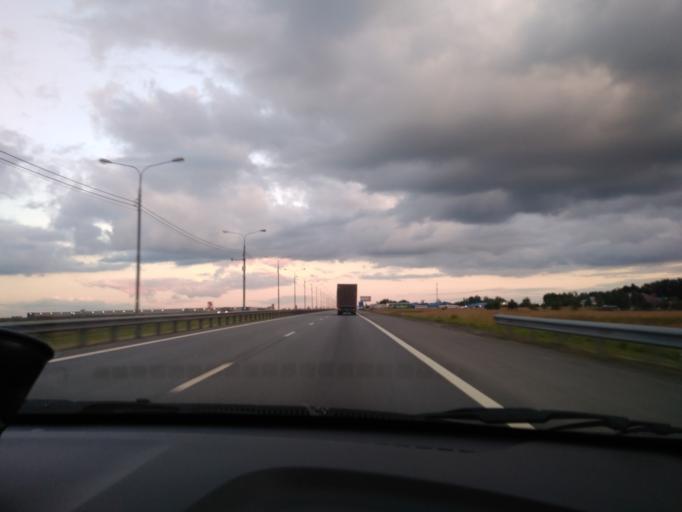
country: RU
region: Moskovskaya
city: Zhukovskiy
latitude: 55.4999
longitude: 38.1463
